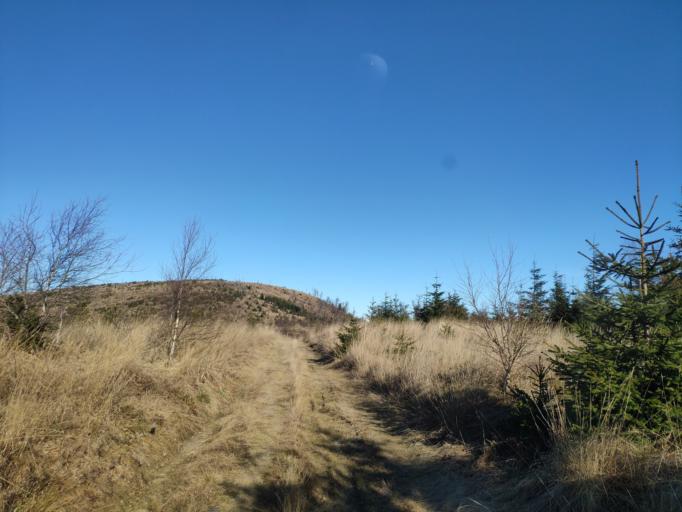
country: SK
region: Kosicky
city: Dobsina
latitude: 48.8234
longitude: 20.4633
